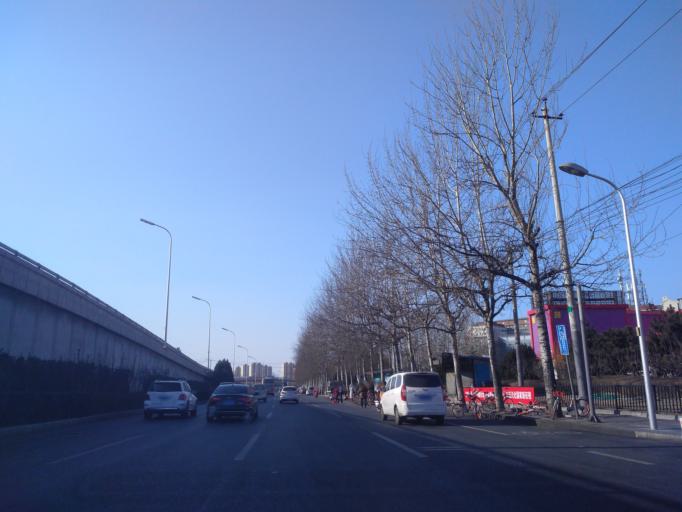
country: CN
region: Beijing
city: Jiugong
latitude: 39.8368
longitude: 116.4654
